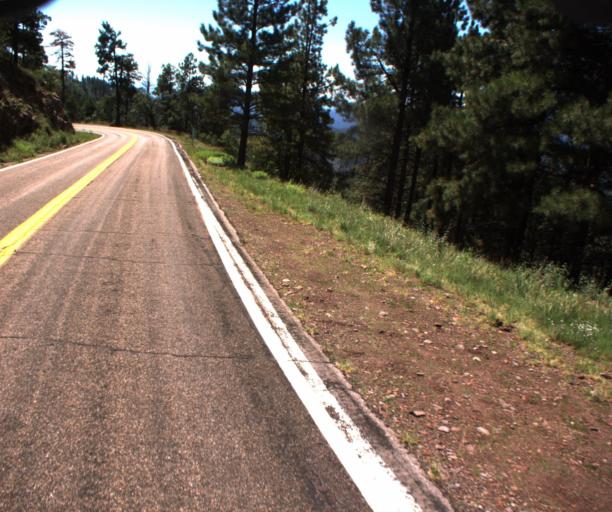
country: US
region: Arizona
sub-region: Greenlee County
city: Morenci
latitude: 33.5708
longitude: -109.3345
